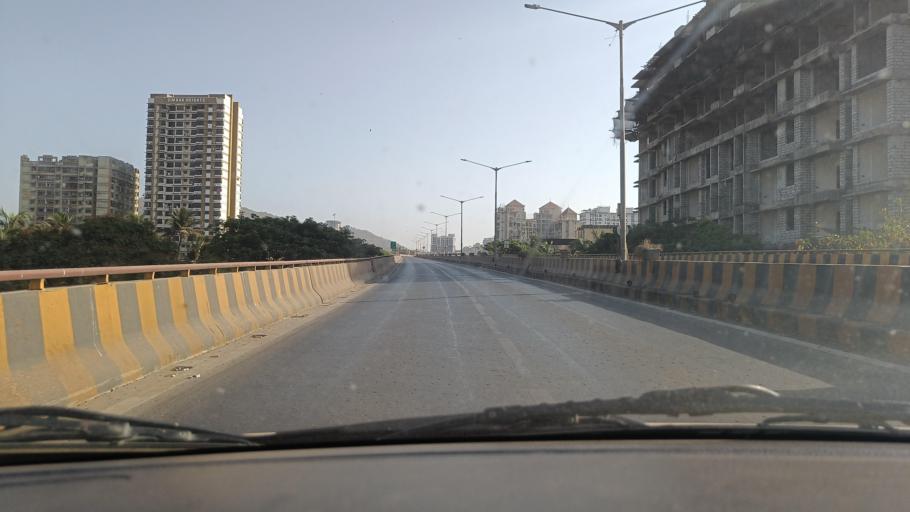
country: IN
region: Maharashtra
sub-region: Mumbai Suburban
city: Mumbai
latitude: 19.0536
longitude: 72.9108
